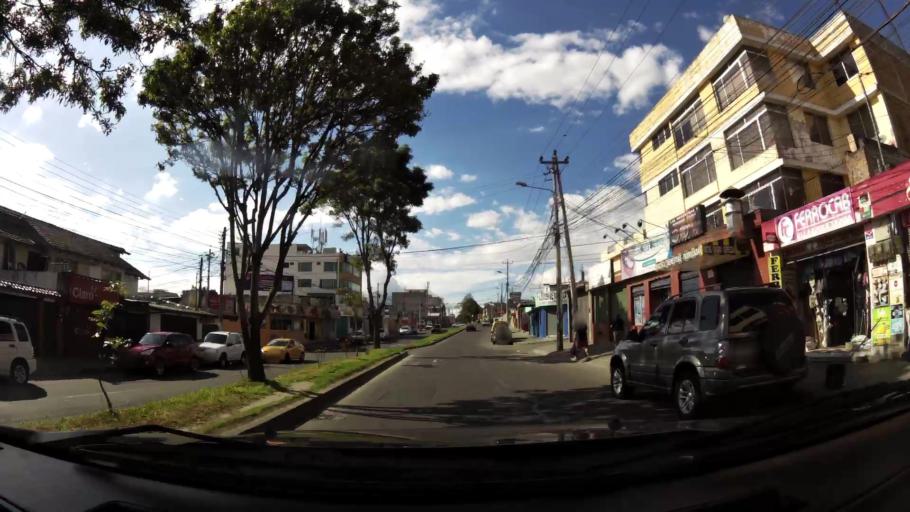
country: EC
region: Pichincha
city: Quito
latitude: -0.1167
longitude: -78.4835
